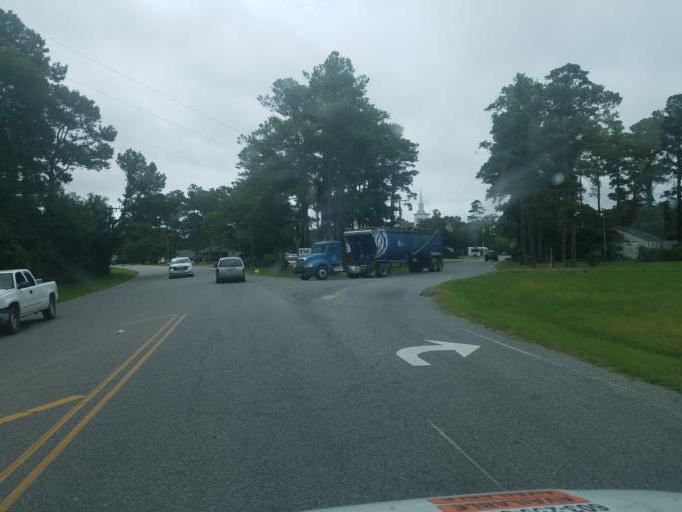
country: US
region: North Carolina
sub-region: Dare County
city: Wanchese
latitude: 35.8497
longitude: -75.6420
